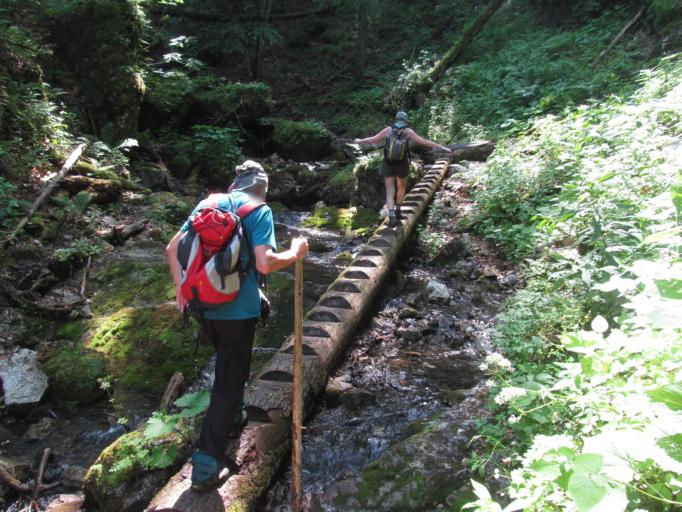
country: SK
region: Kosicky
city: Dobsina
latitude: 48.9191
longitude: 20.3637
